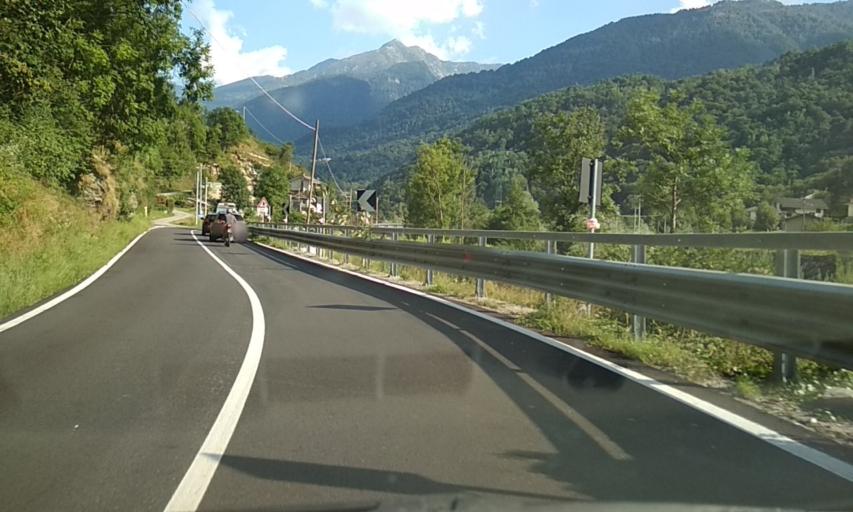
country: IT
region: Piedmont
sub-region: Provincia di Torino
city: Locana
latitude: 45.4224
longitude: 7.4435
